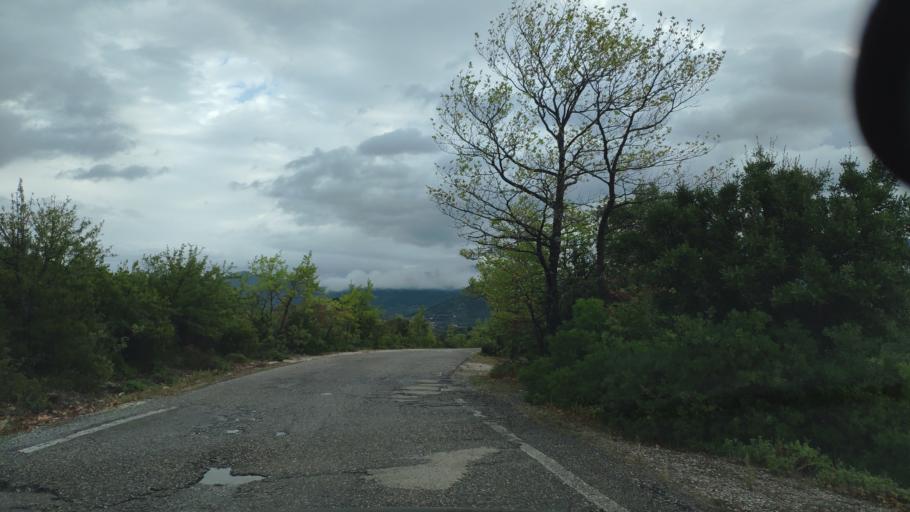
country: GR
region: West Greece
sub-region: Nomos Aitolias kai Akarnanias
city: Sardinia
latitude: 38.8451
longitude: 21.3227
